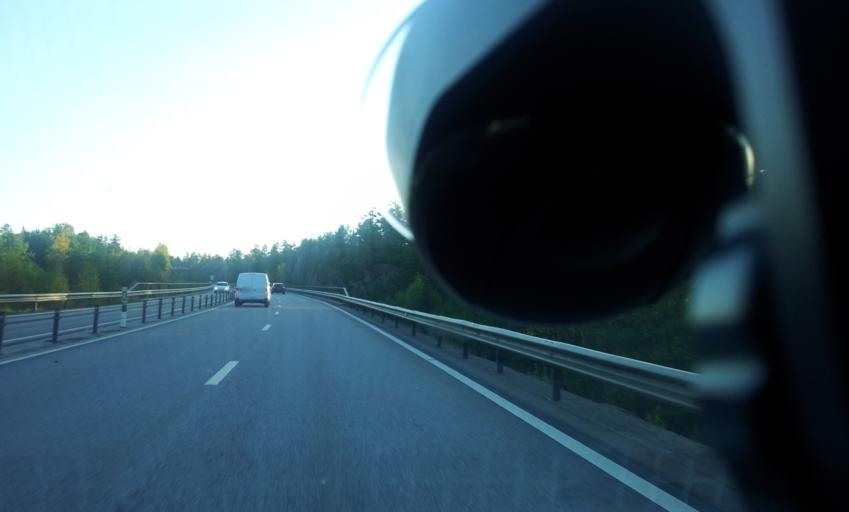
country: SE
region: Kalmar
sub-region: Vasterviks Kommun
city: Vaestervik
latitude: 57.7420
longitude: 16.5537
